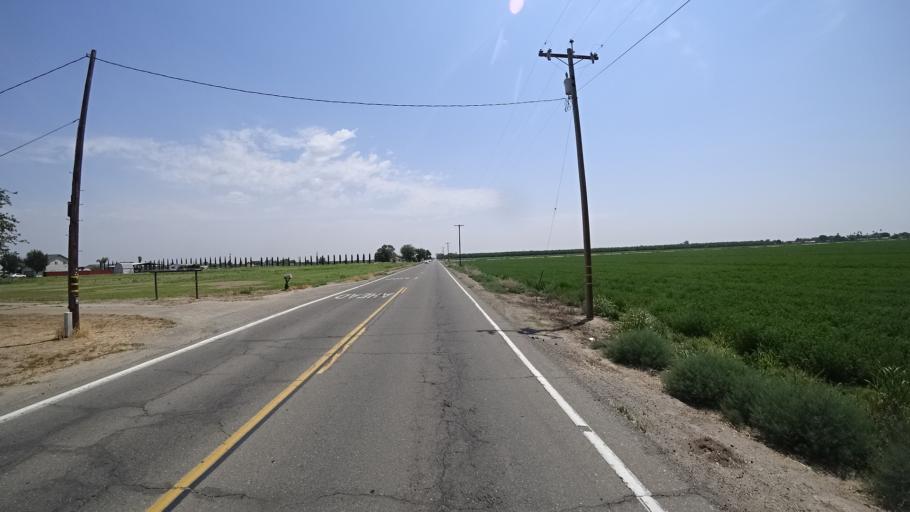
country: US
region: California
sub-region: Kings County
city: Lemoore
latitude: 36.3280
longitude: -119.7795
